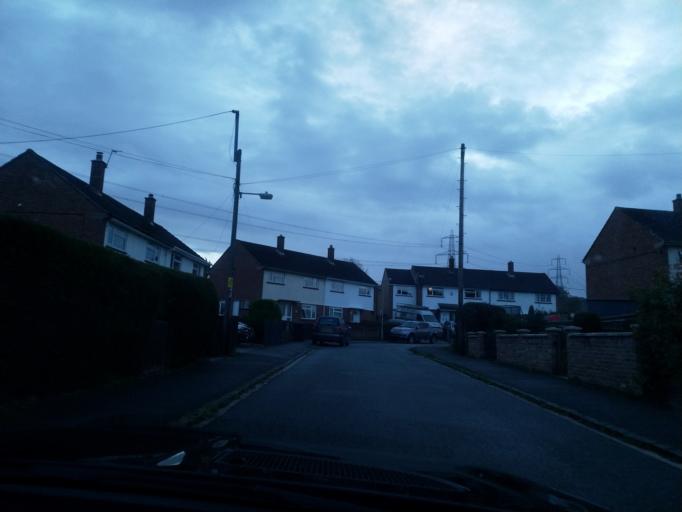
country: GB
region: England
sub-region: Oxfordshire
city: Wheatley
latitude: 51.7428
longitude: -1.1264
